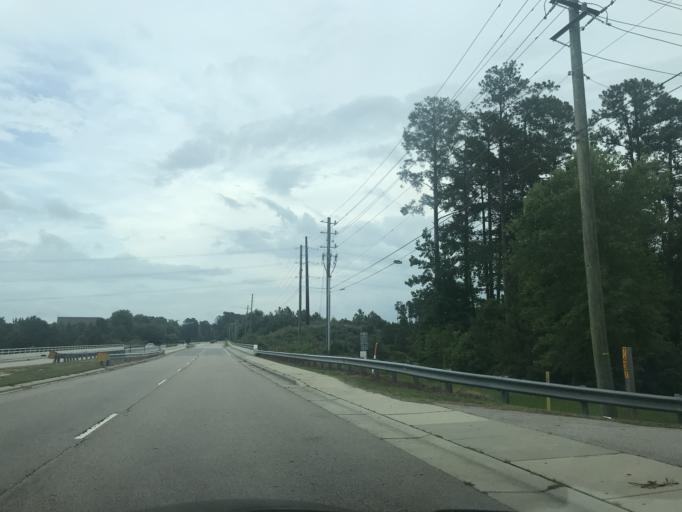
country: US
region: North Carolina
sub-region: Wake County
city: Green Level
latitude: 35.8226
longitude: -78.8944
